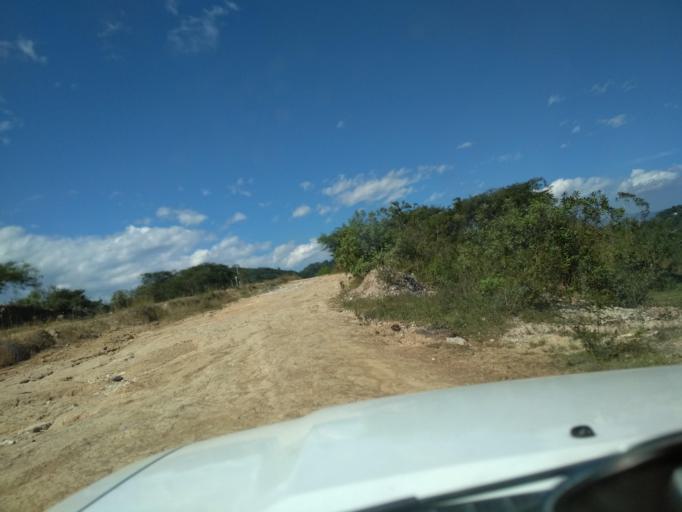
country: MX
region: Veracruz
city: El Castillo
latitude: 19.5469
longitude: -96.8541
